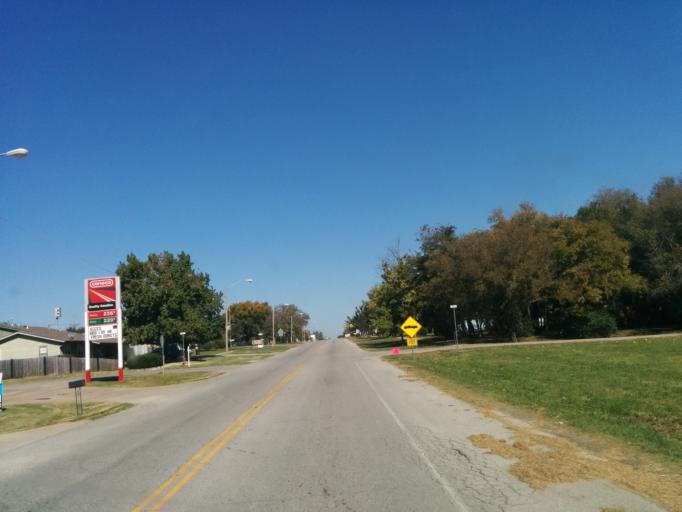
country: US
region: Oklahoma
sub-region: Creek County
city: Mounds
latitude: 35.8719
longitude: -96.0607
